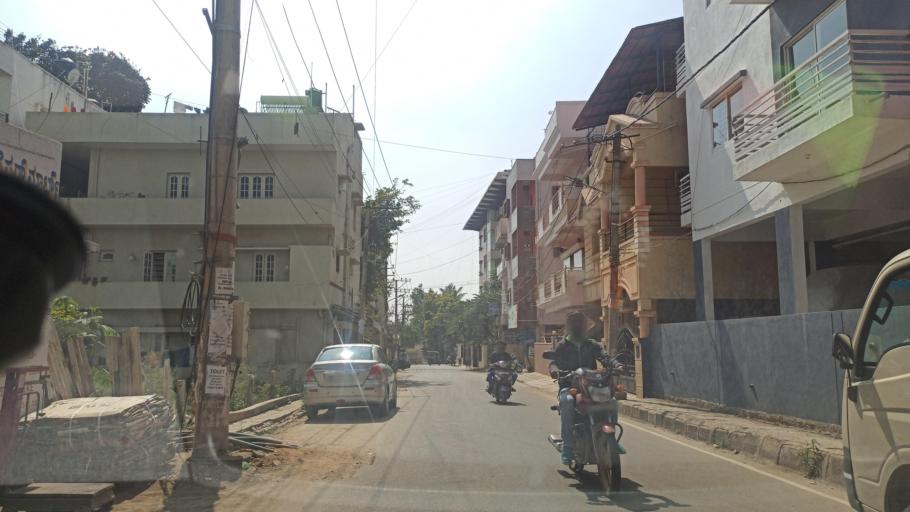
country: IN
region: Karnataka
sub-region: Bangalore Urban
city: Yelahanka
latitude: 13.0546
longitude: 77.5993
